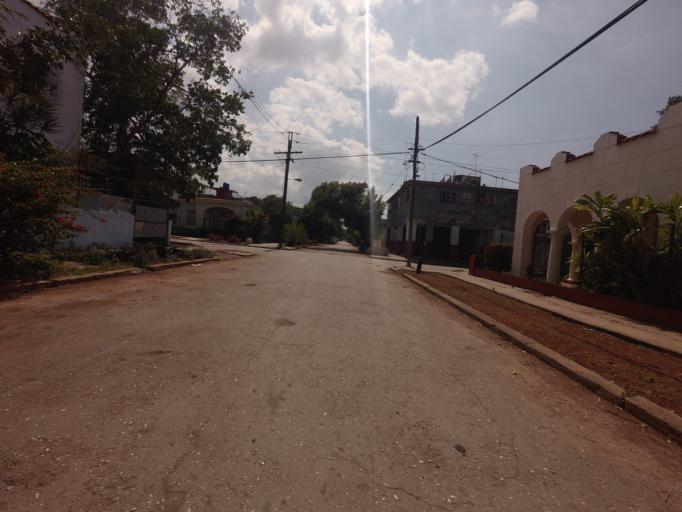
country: CU
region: La Habana
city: Cerro
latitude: 23.1059
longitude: -82.4276
